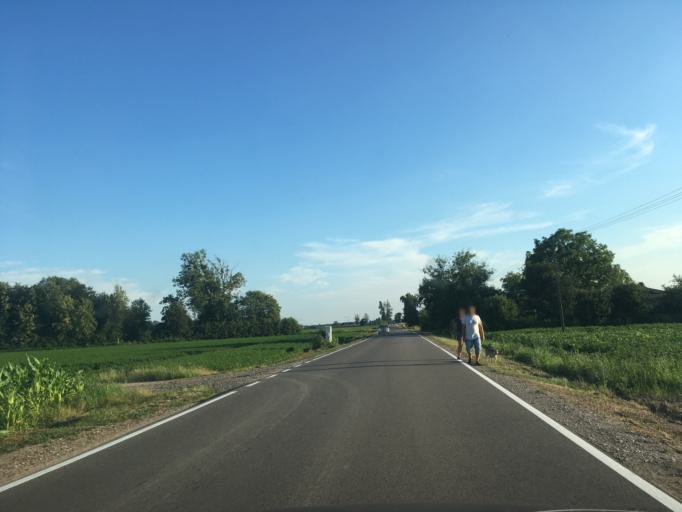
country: PL
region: Masovian Voivodeship
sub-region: Powiat warszawski zachodni
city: Bieniewice
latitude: 52.1383
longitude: 20.5919
